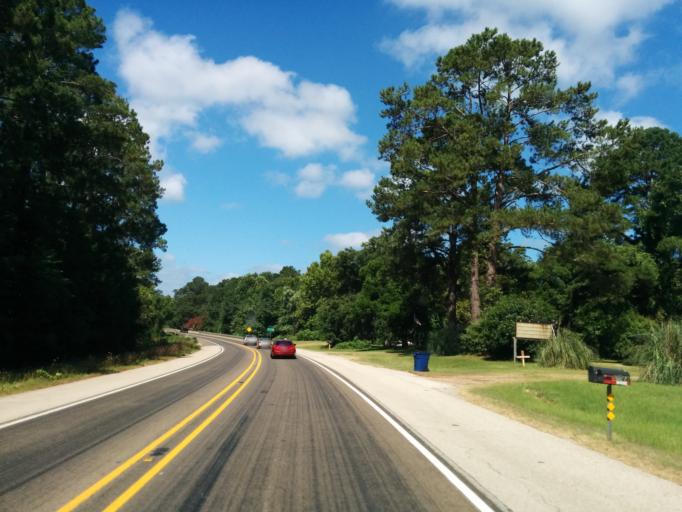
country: US
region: Texas
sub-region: Angelina County
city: Hudson
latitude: 31.3985
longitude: -94.9620
